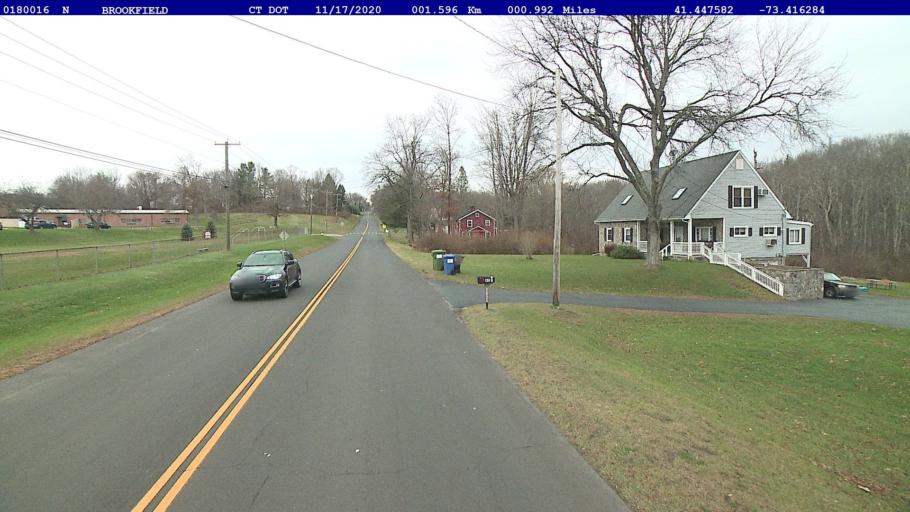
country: US
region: Connecticut
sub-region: Fairfield County
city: Danbury
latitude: 41.4476
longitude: -73.4163
